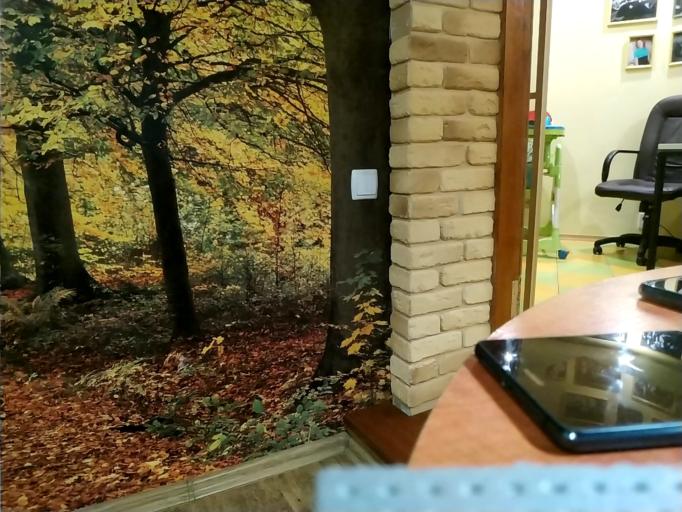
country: RU
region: Tverskaya
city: Zubtsov
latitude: 56.2161
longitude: 34.7121
